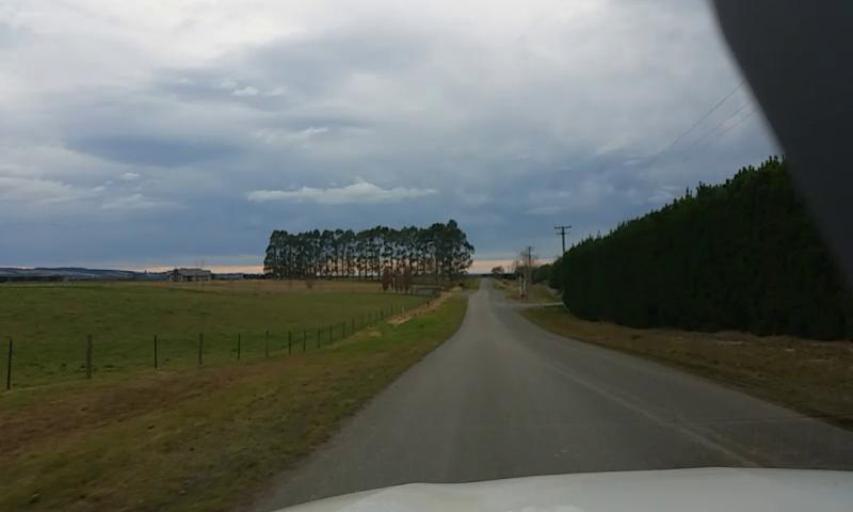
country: NZ
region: Canterbury
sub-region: Waimakariri District
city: Kaiapoi
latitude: -43.2911
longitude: 172.4599
